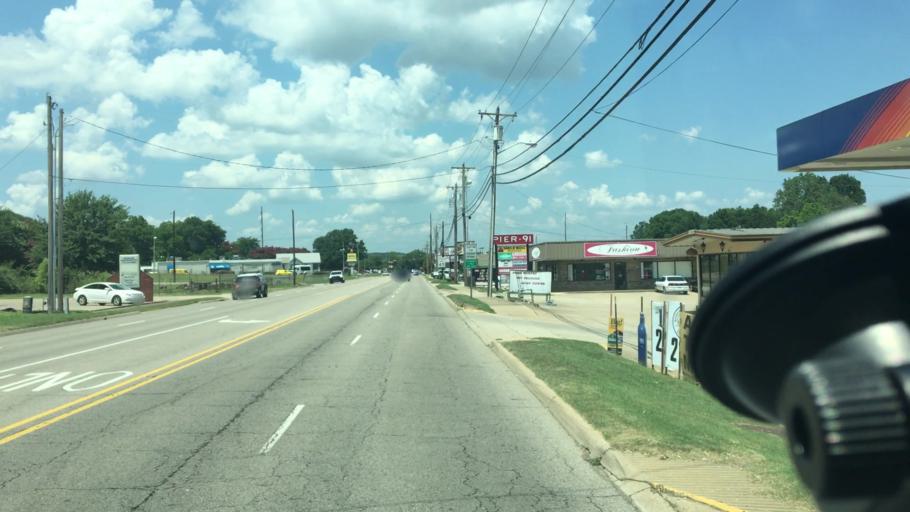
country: US
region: Arkansas
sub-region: Sebastian County
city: Barling
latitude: 35.3453
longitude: -94.3321
